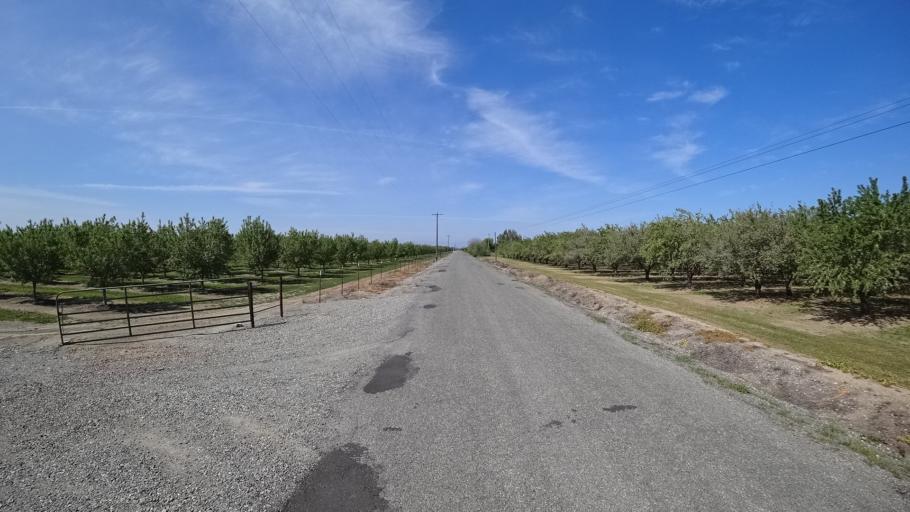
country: US
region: California
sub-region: Glenn County
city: Hamilton City
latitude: 39.8042
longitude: -122.0859
